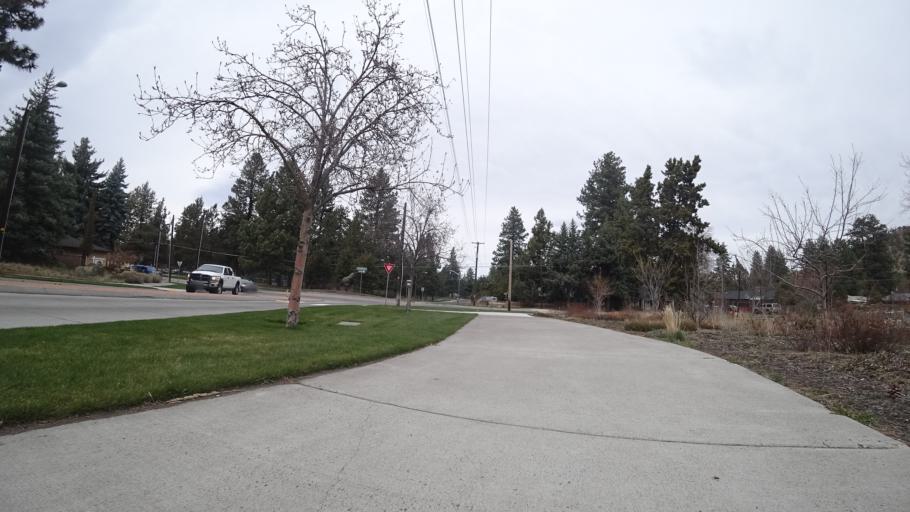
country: US
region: Oregon
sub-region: Deschutes County
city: Bend
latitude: 44.0555
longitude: -121.2936
